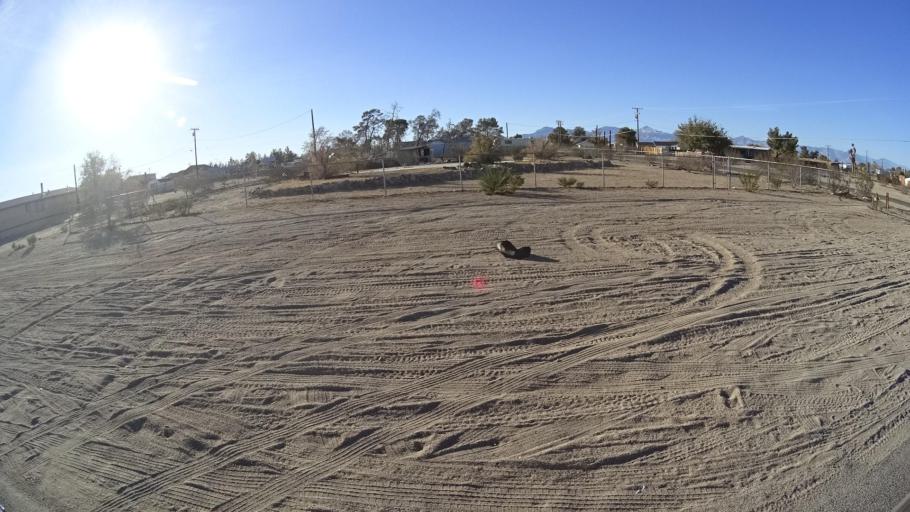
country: US
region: California
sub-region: Kern County
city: Ridgecrest
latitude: 35.6005
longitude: -117.6969
